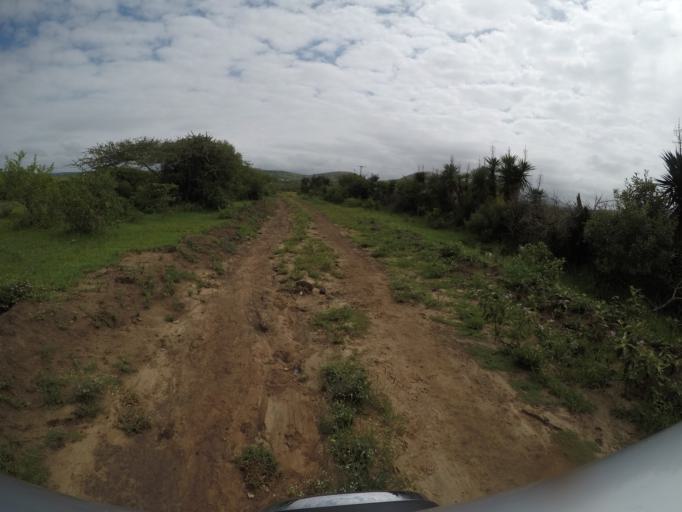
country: ZA
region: KwaZulu-Natal
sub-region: uThungulu District Municipality
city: Empangeni
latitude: -28.6224
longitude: 31.8653
